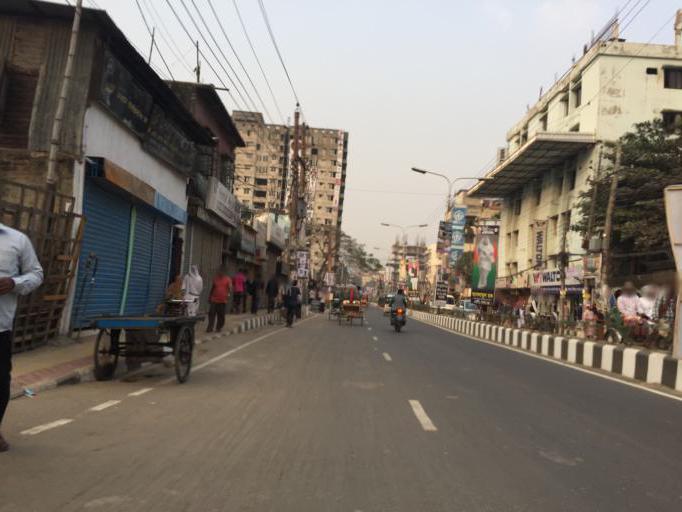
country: BD
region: Dhaka
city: Azimpur
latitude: 23.7929
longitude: 90.3486
